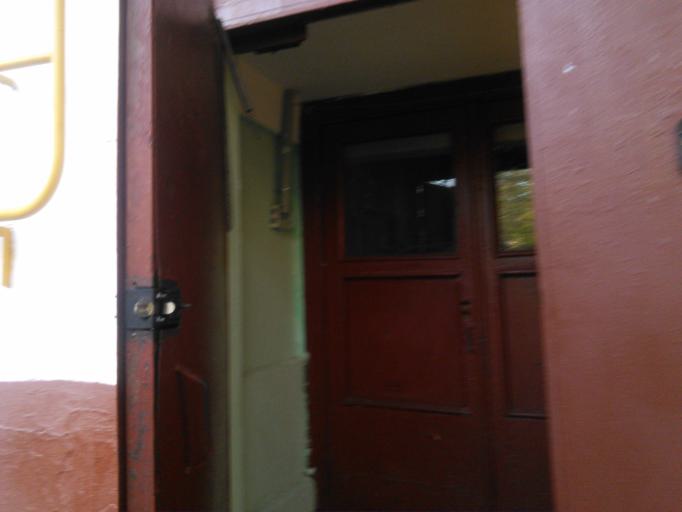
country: RU
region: Moskovskaya
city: Khoroshevo-Mnevniki
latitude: 55.7714
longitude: 37.4720
